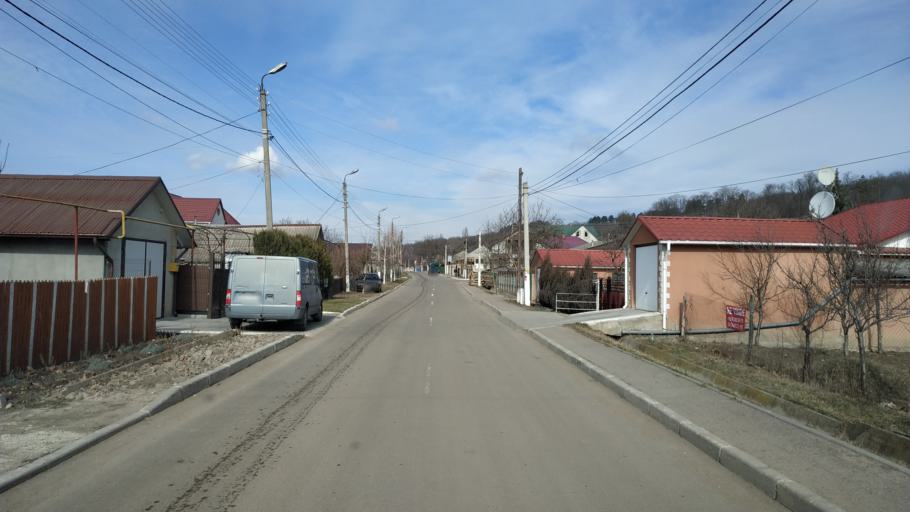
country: MD
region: Hincesti
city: Hincesti
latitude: 46.8302
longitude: 28.6046
